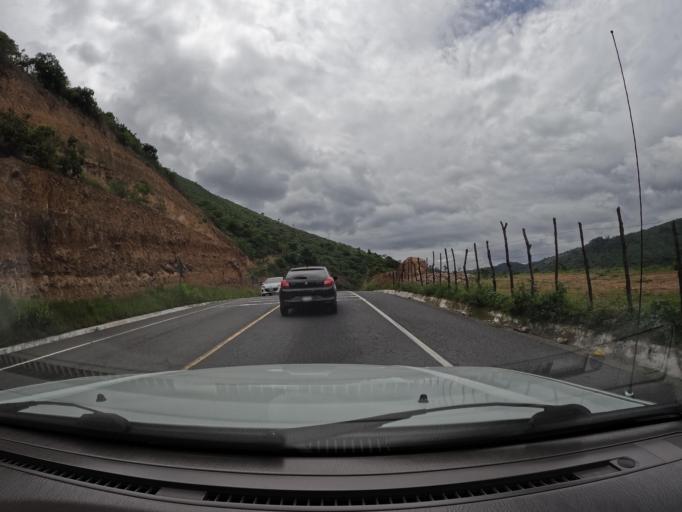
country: GT
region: Sacatepequez
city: Jocotenango
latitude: 14.5818
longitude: -90.7505
